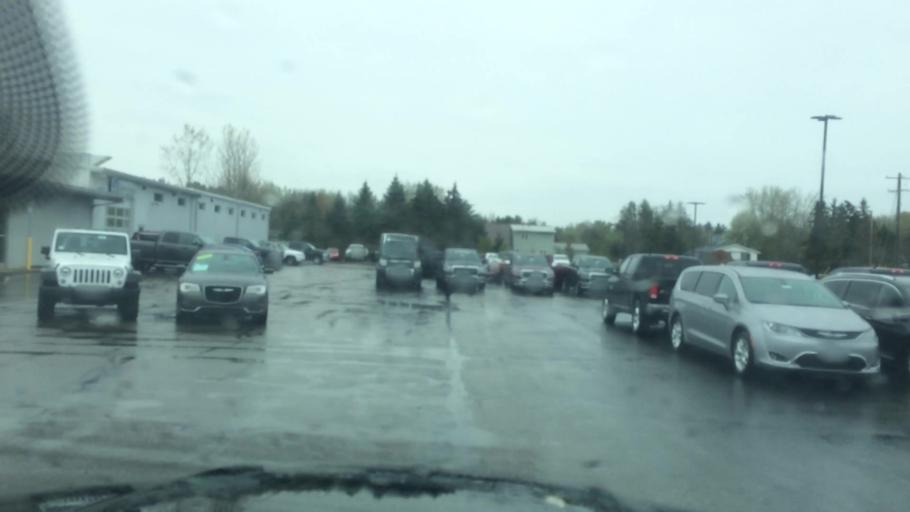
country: US
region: Wisconsin
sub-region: Portage County
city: Whiting
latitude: 44.5231
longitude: -89.5170
